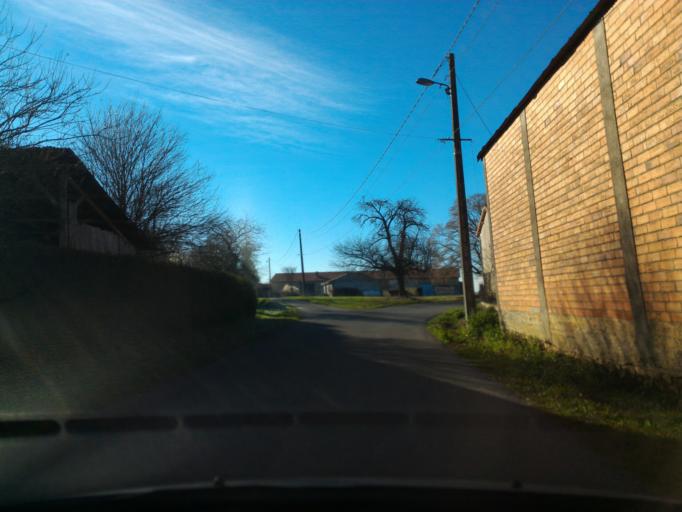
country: FR
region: Poitou-Charentes
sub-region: Departement de la Charente
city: Champagne-Mouton
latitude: 45.9709
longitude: 0.3935
